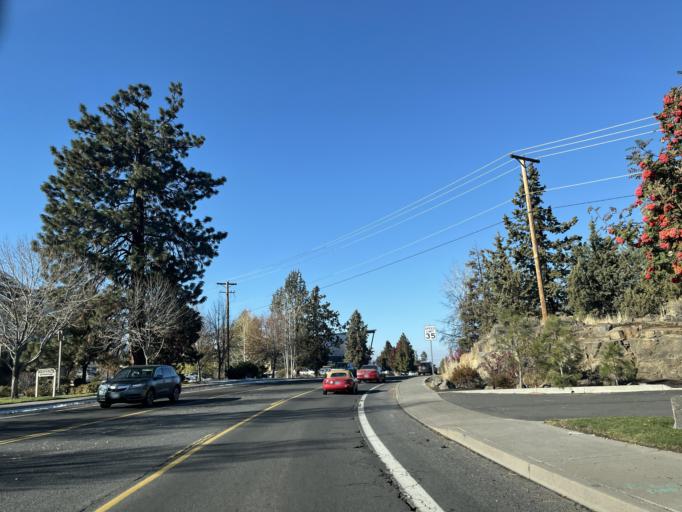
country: US
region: Oregon
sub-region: Deschutes County
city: Bend
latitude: 44.0764
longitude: -121.2974
